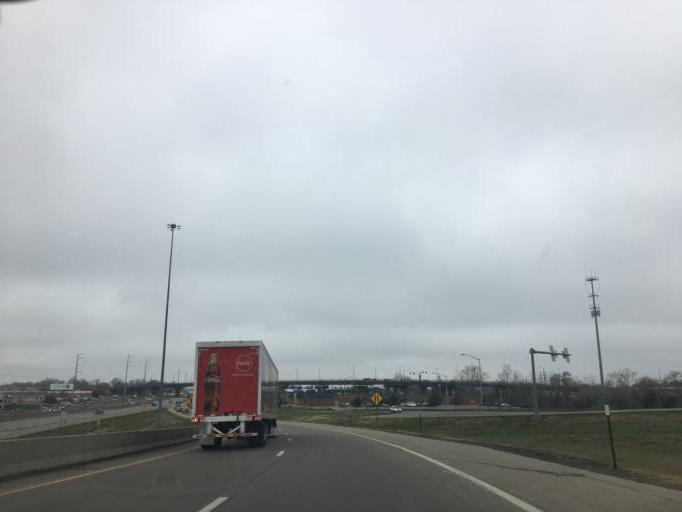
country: US
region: Kansas
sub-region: Johnson County
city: Lenexa
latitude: 38.9705
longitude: -94.7202
